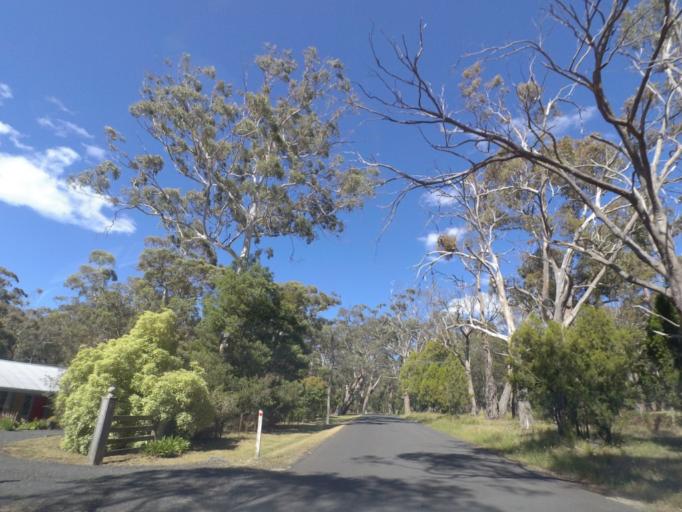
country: AU
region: Victoria
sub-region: Hume
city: Sunbury
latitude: -37.4206
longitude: 144.6245
